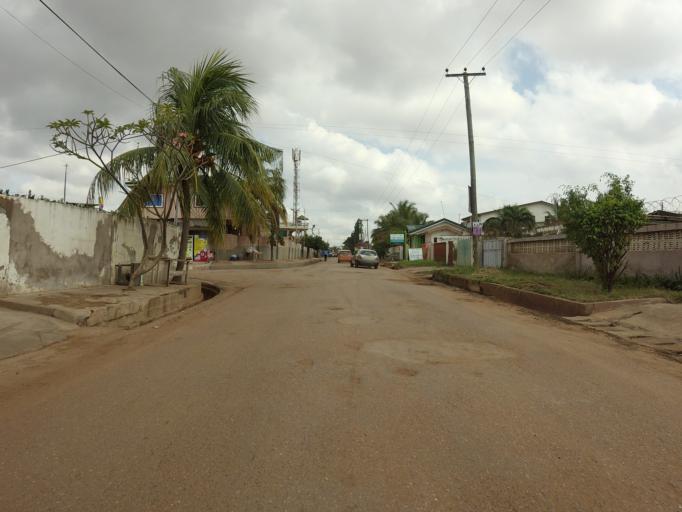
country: GH
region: Greater Accra
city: Nungua
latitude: 5.6160
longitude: -0.1011
